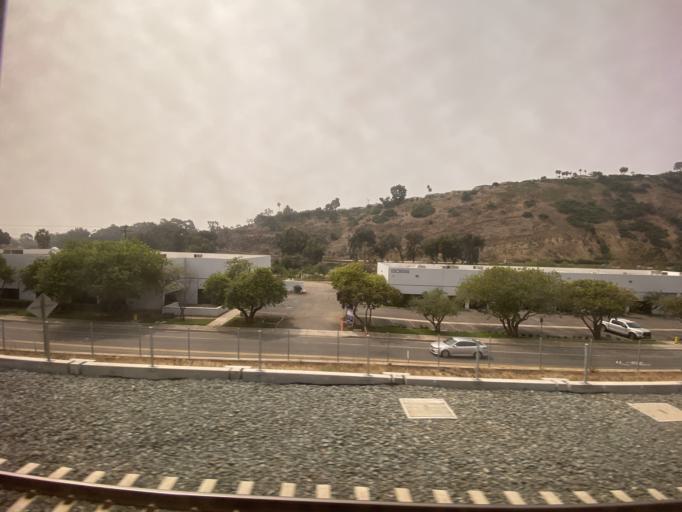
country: US
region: California
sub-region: San Diego County
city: La Jolla
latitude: 32.8144
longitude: -117.2195
